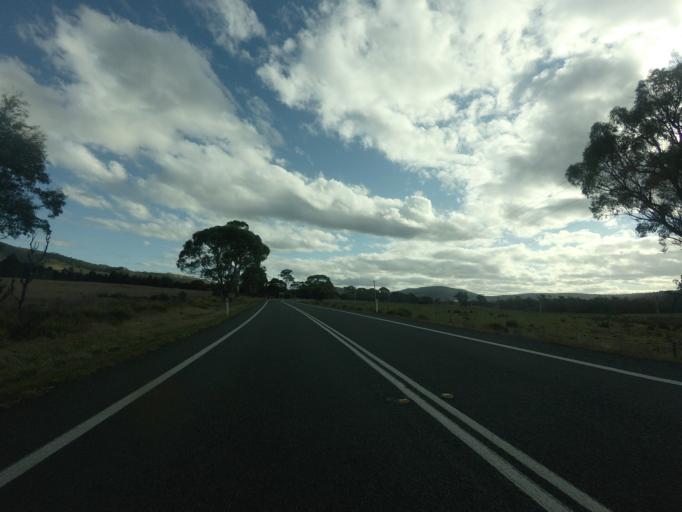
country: AU
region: Tasmania
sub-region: Sorell
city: Sorell
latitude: -42.6384
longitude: 147.5882
